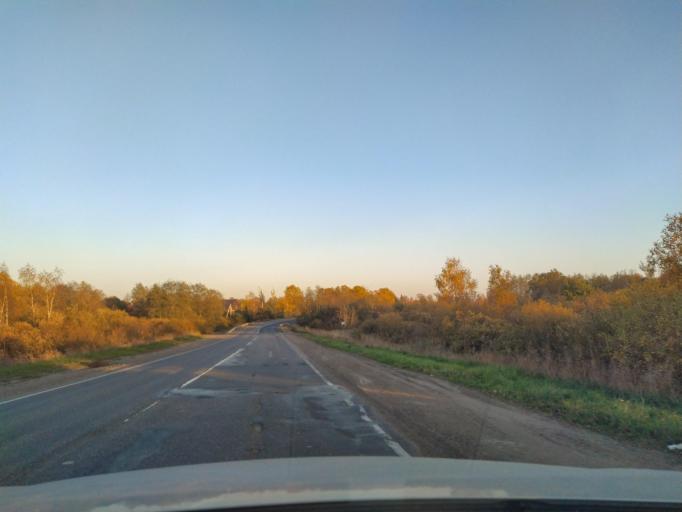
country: RU
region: Leningrad
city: Maloye Verevo
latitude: 59.6162
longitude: 30.2132
